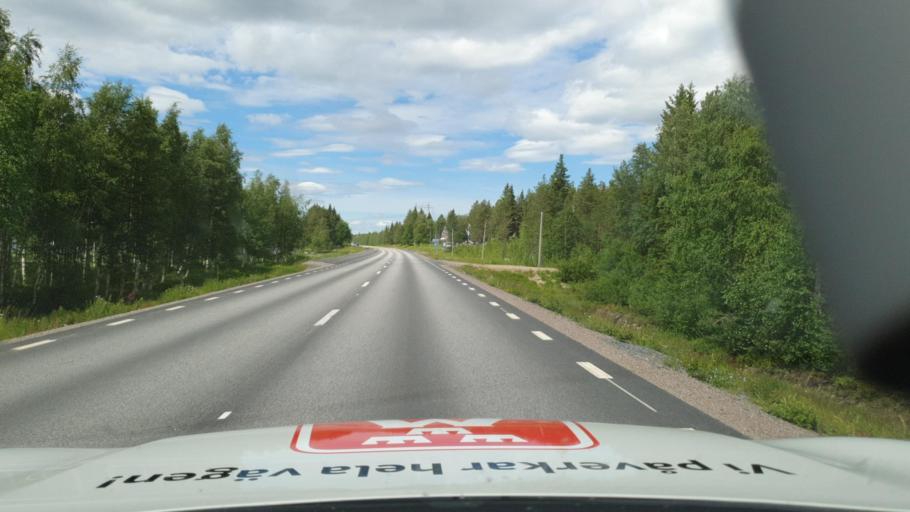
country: SE
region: Vaesterbotten
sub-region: Norsjo Kommun
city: Norsjoe
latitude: 65.1896
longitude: 19.8430
